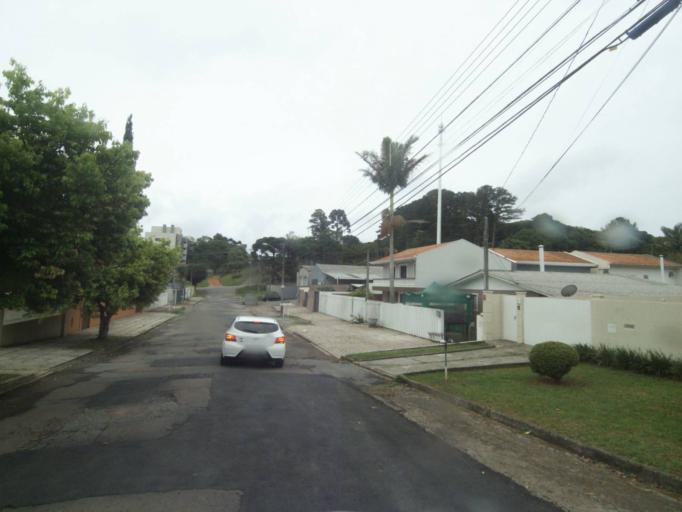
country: BR
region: Parana
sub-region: Curitiba
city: Curitiba
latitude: -25.4280
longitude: -49.3300
